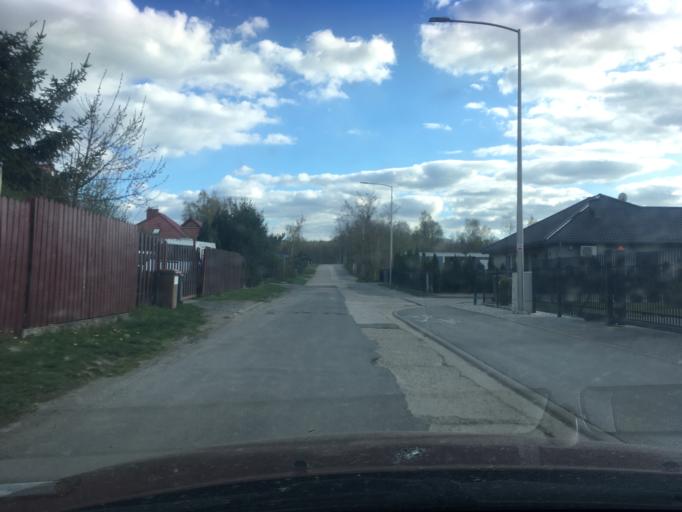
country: PL
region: Lower Silesian Voivodeship
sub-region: Powiat zgorzelecki
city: Zgorzelec
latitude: 51.1286
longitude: 15.0048
